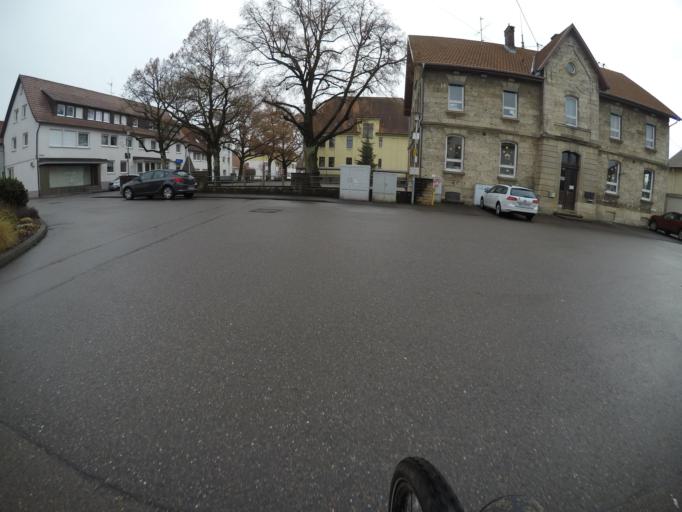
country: DE
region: Baden-Wuerttemberg
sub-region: Regierungsbezirk Stuttgart
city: Frickenhausen
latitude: 48.5917
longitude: 9.3600
